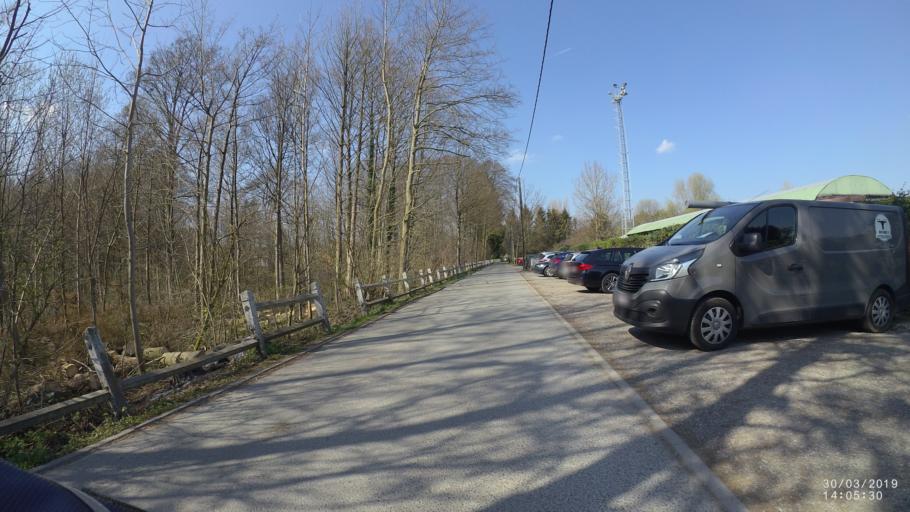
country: BE
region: Wallonia
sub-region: Province du Brabant Wallon
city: Louvain-la-Neuve
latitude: 50.6820
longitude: 4.6140
